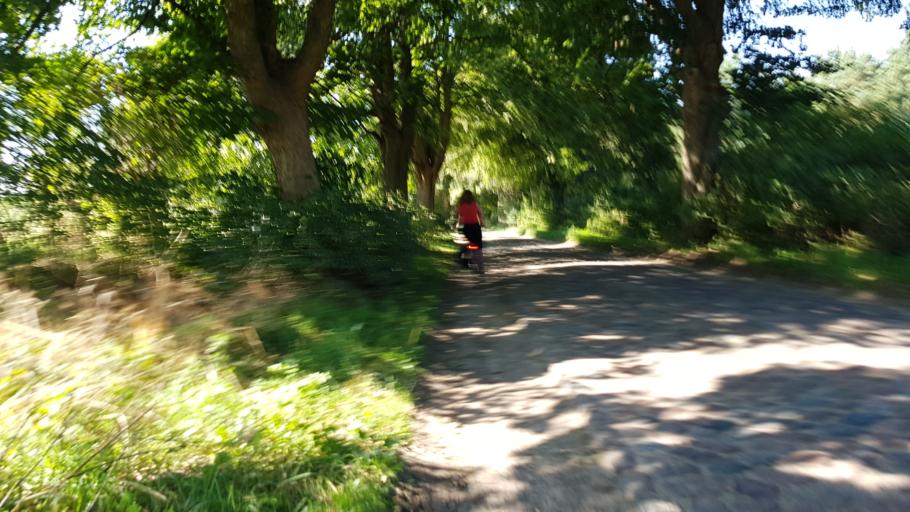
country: PL
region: West Pomeranian Voivodeship
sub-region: Powiat gryfinski
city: Gryfino
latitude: 53.1551
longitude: 14.4989
